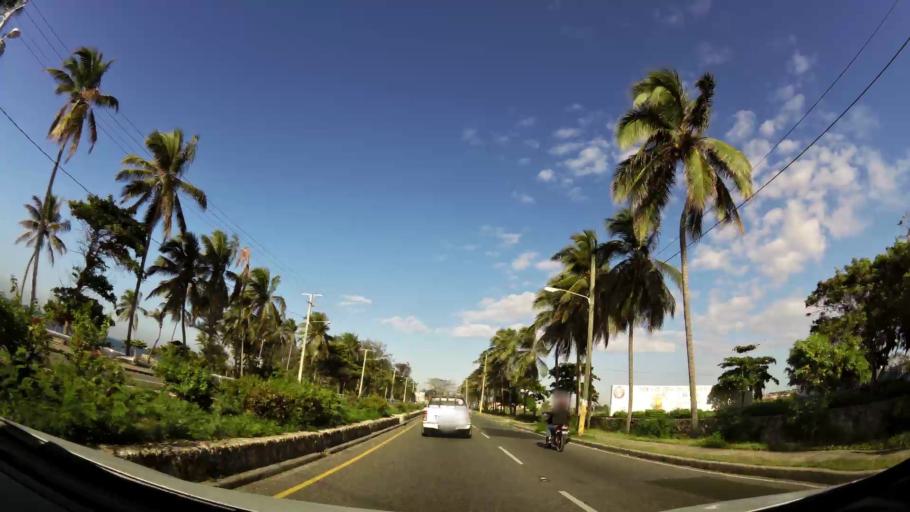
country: DO
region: Santo Domingo
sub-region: Santo Domingo
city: Santo Domingo Este
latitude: 18.4688
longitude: -69.8533
